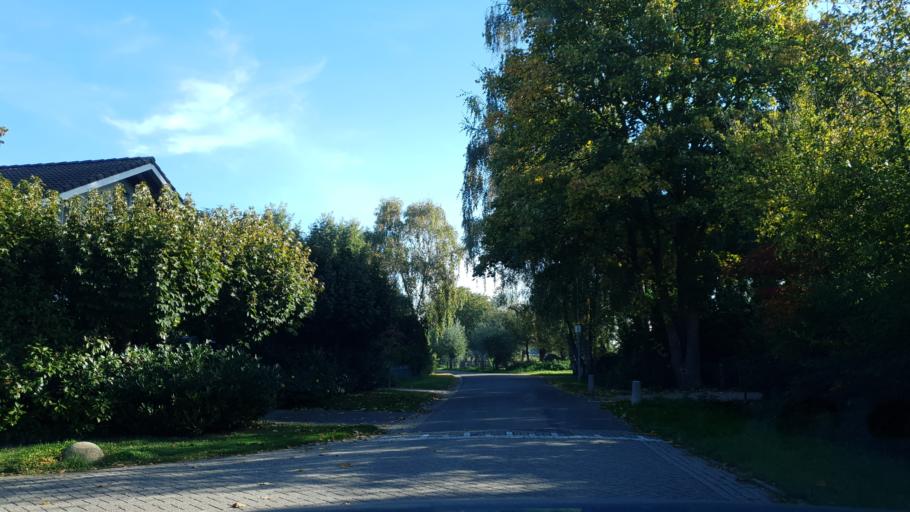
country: NL
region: Gelderland
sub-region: Gemeente Beuningen
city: Beuningen
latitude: 51.8574
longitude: 5.7836
